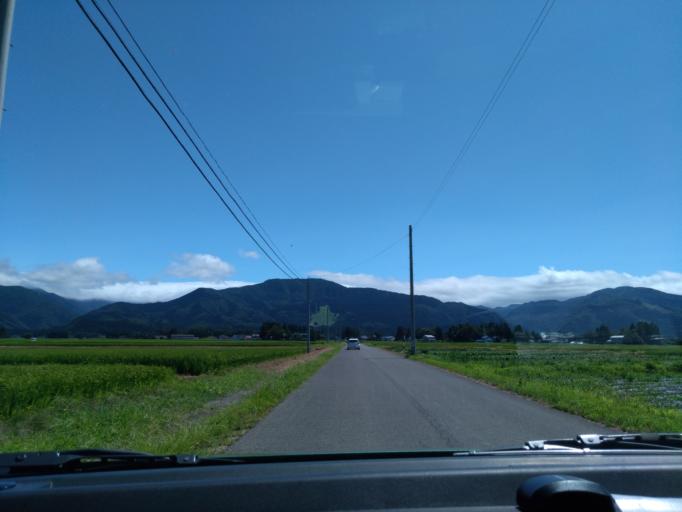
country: JP
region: Akita
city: Kakunodatemachi
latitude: 39.5267
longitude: 140.6163
